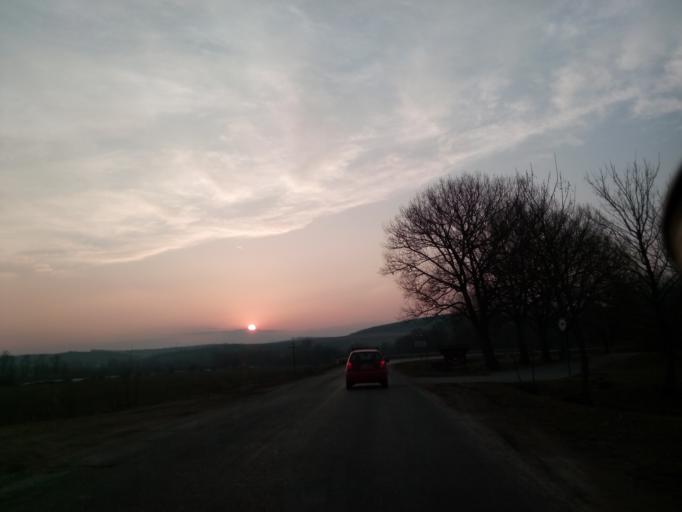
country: HU
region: Borsod-Abauj-Zemplen
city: Gonc
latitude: 48.4968
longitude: 21.2333
